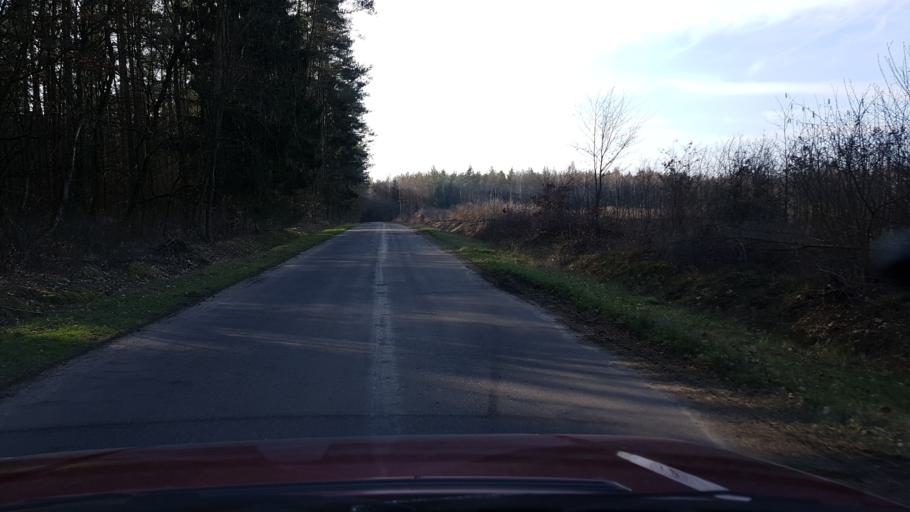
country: PL
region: West Pomeranian Voivodeship
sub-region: Powiat gryficki
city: Ploty
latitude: 53.8316
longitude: 15.3167
